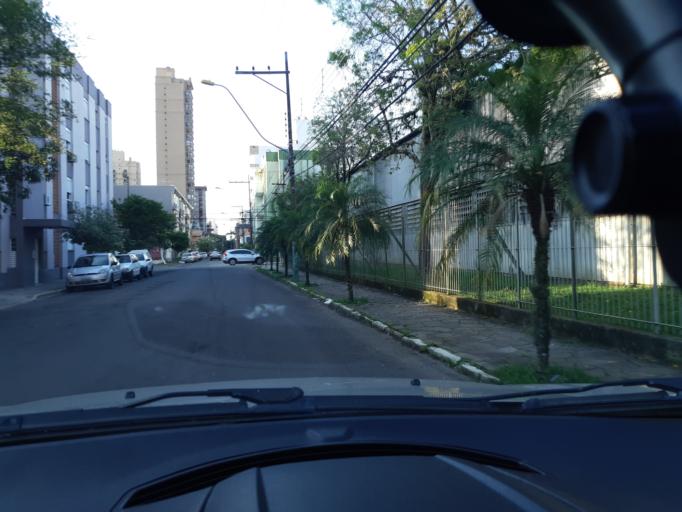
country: BR
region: Rio Grande do Sul
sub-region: Sao Leopoldo
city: Sao Leopoldo
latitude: -29.7657
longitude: -51.1416
